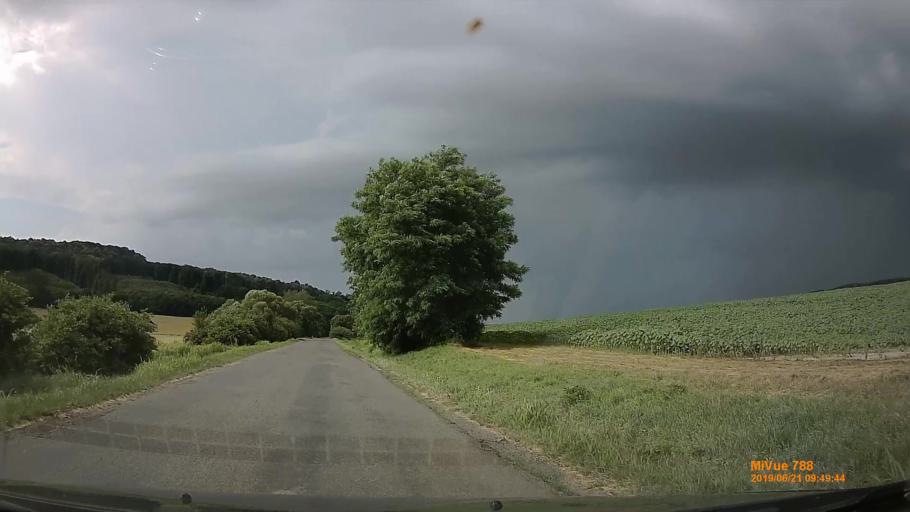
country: HU
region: Baranya
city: Sasd
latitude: 46.2659
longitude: 18.0358
